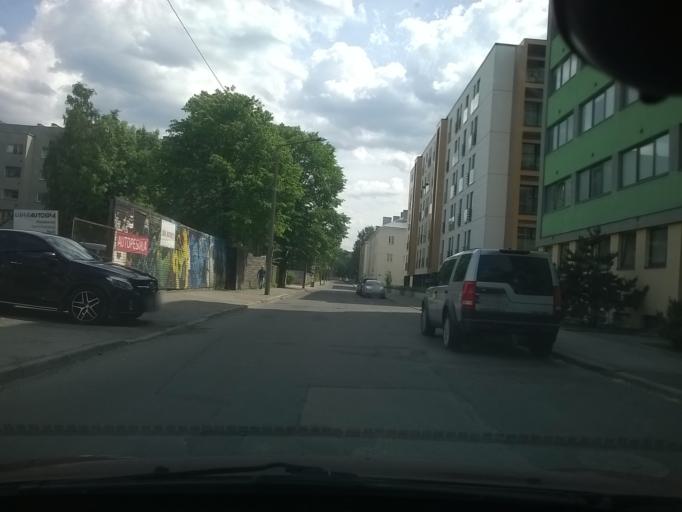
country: EE
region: Harju
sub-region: Tallinna linn
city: Tallinn
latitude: 59.4252
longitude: 24.7352
